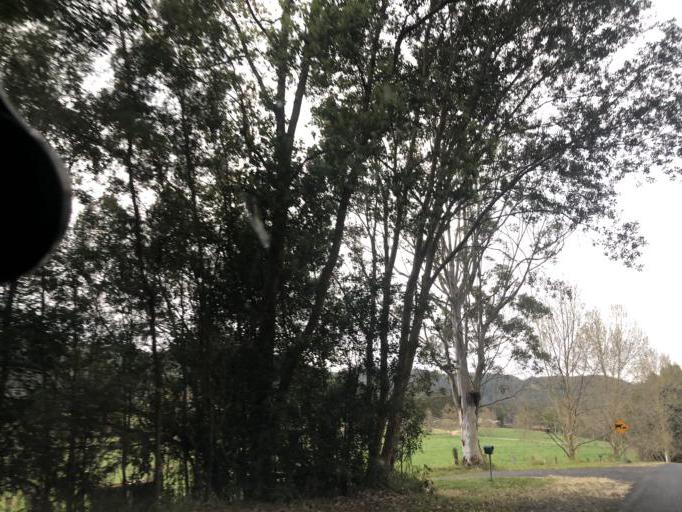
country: AU
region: New South Wales
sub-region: Coffs Harbour
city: Boambee
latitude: -30.2635
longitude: 153.0107
